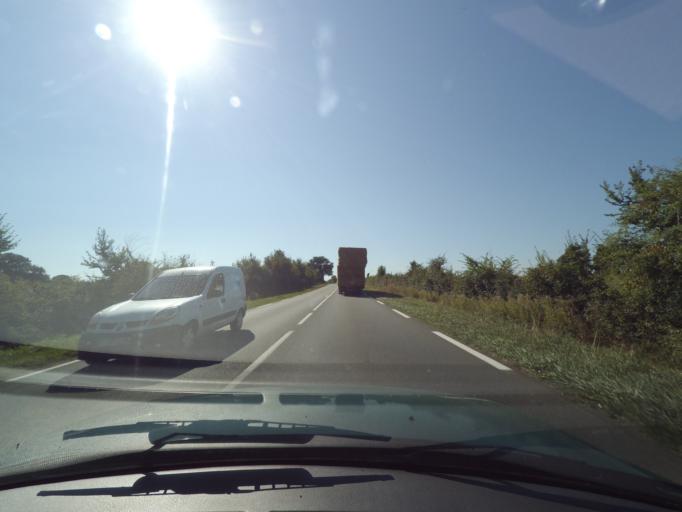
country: FR
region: Poitou-Charentes
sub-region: Departement de la Vienne
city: Lussac-les-Chateaux
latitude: 46.3886
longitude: 0.7413
